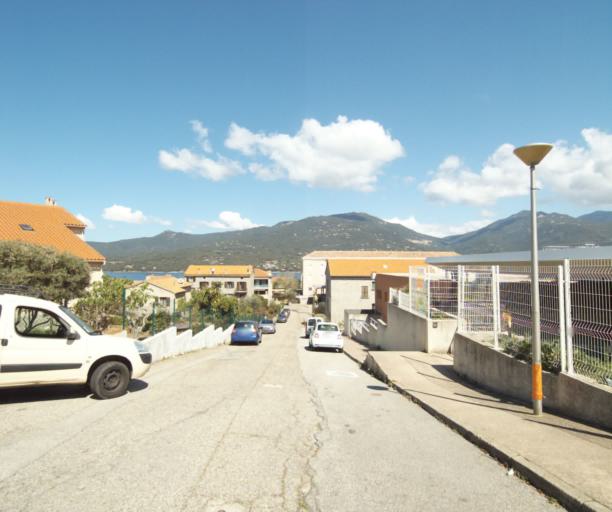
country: FR
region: Corsica
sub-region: Departement de la Corse-du-Sud
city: Propriano
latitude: 41.6746
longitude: 8.9072
